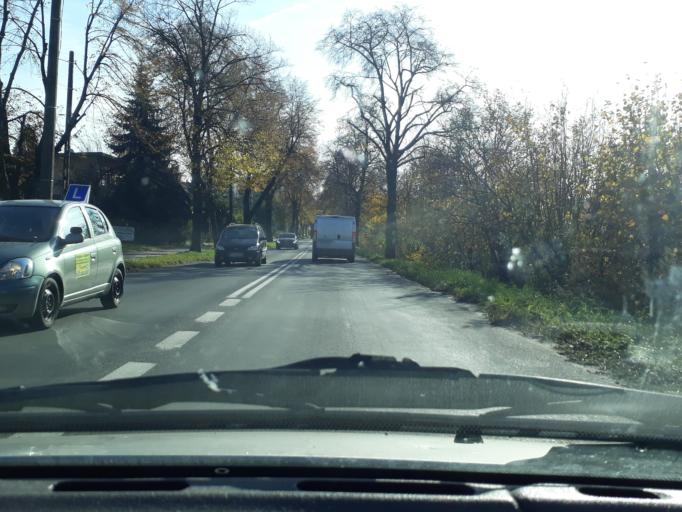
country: PL
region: Silesian Voivodeship
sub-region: Powiat tarnogorski
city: Tarnowskie Gory
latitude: 50.4370
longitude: 18.8626
